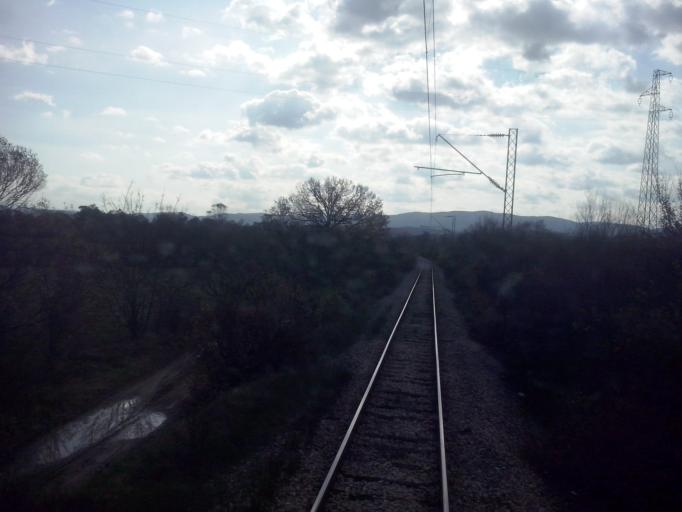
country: RS
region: Central Serbia
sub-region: Zlatiborski Okrug
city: Pozega
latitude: 43.8561
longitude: 20.0157
